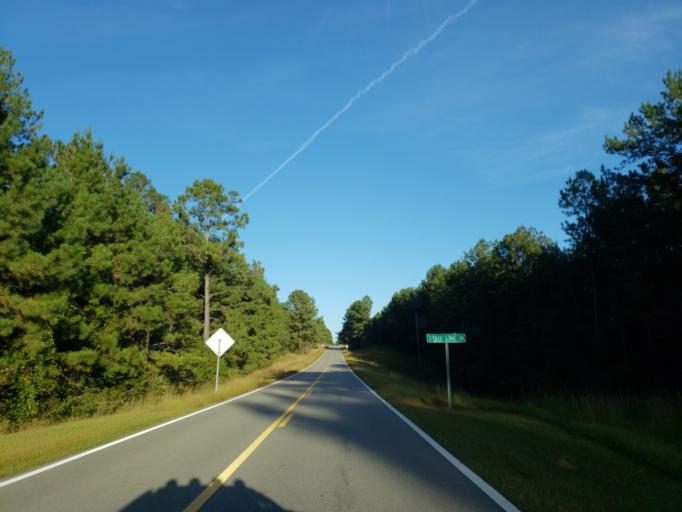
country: US
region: Mississippi
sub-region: Perry County
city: Richton
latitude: 31.3546
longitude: -88.7558
